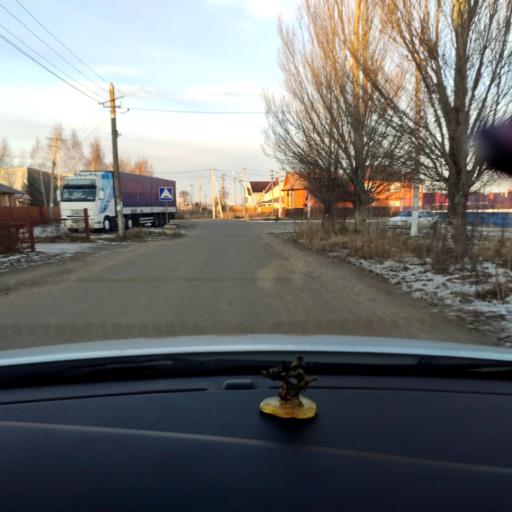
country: RU
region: Tatarstan
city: Stolbishchi
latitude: 55.6093
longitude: 49.1486
